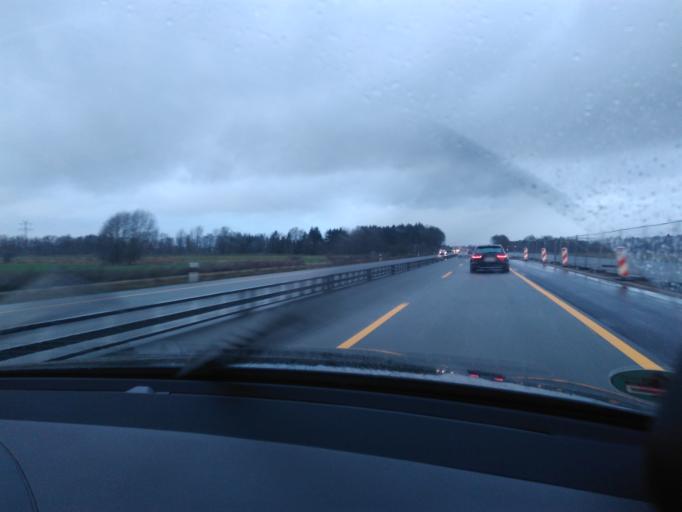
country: DE
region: Schleswig-Holstein
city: Grossenaspe
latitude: 53.9713
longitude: 9.9484
